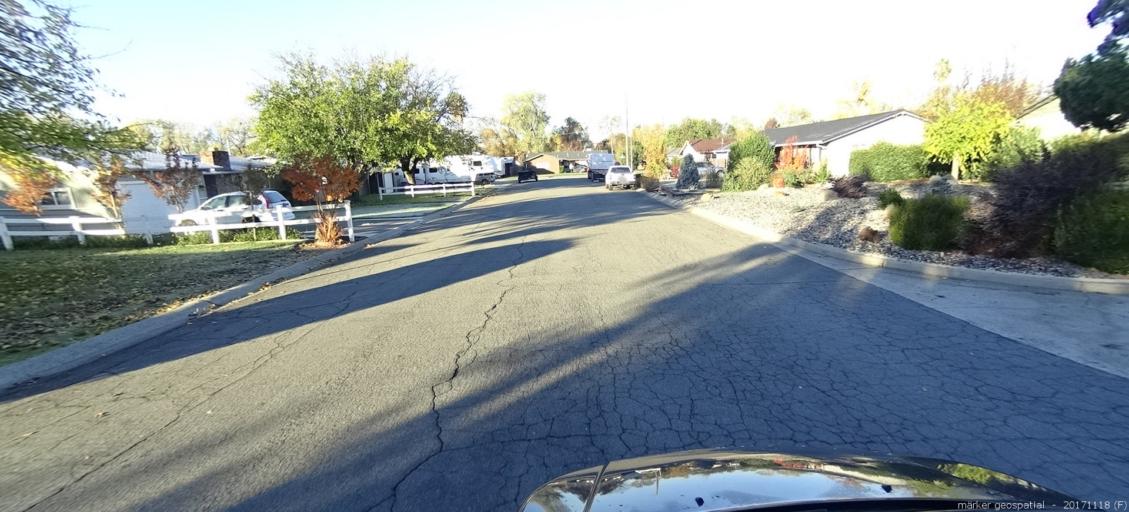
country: US
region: California
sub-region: Shasta County
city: Cottonwood
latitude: 40.3899
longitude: -122.2892
